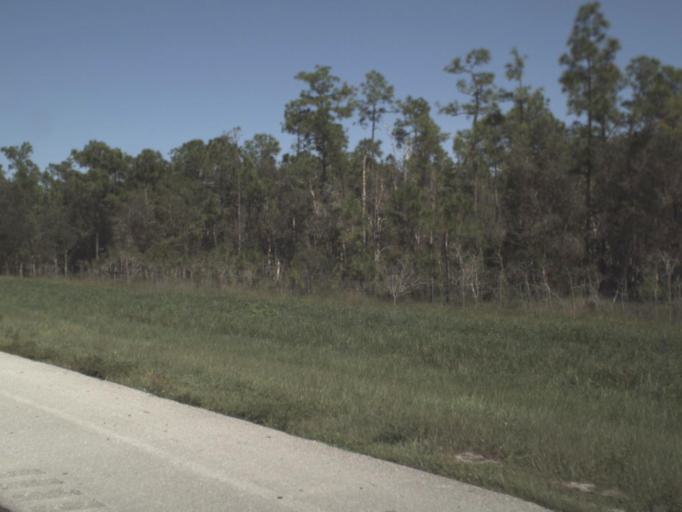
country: US
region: Florida
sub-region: Lee County
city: Estero
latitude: 26.4042
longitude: -81.7726
